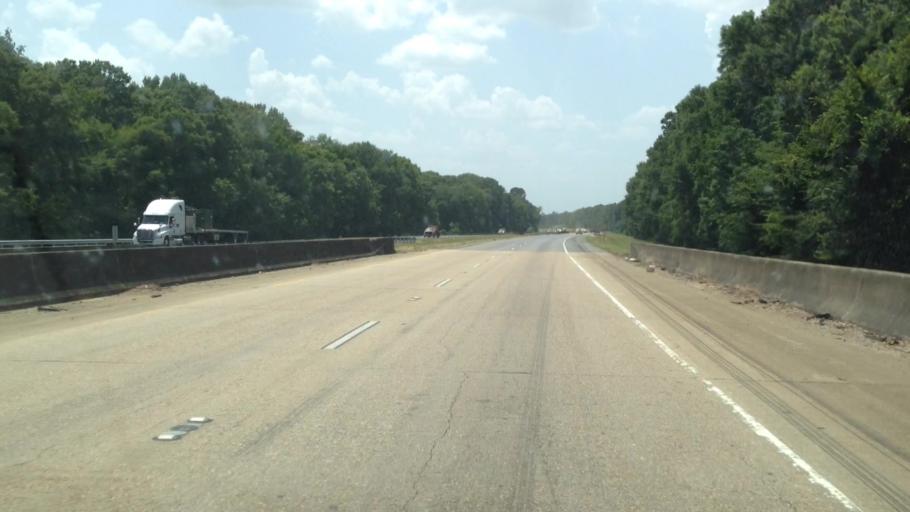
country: US
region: Louisiana
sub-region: Lincoln Parish
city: Ruston
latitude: 32.5253
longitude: -92.4325
